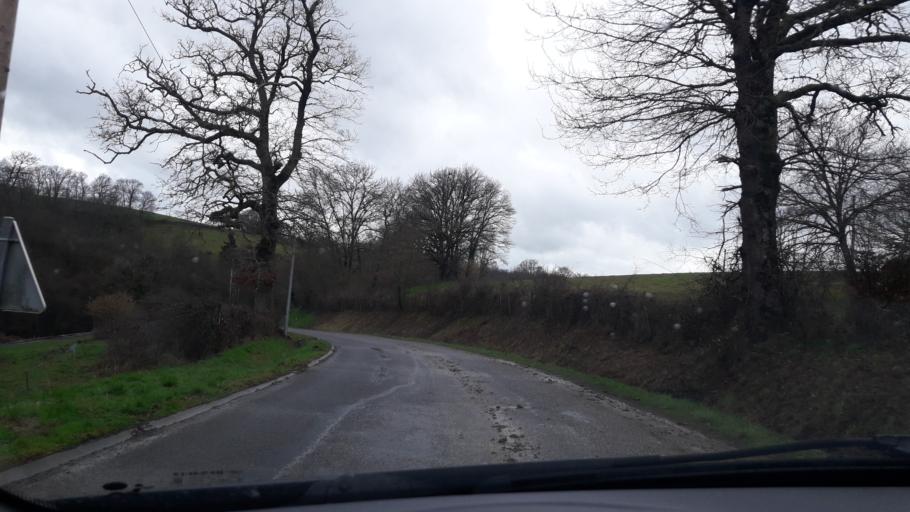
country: FR
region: Limousin
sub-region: Departement de la Haute-Vienne
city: Pierre-Buffiere
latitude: 45.7307
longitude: 1.3864
